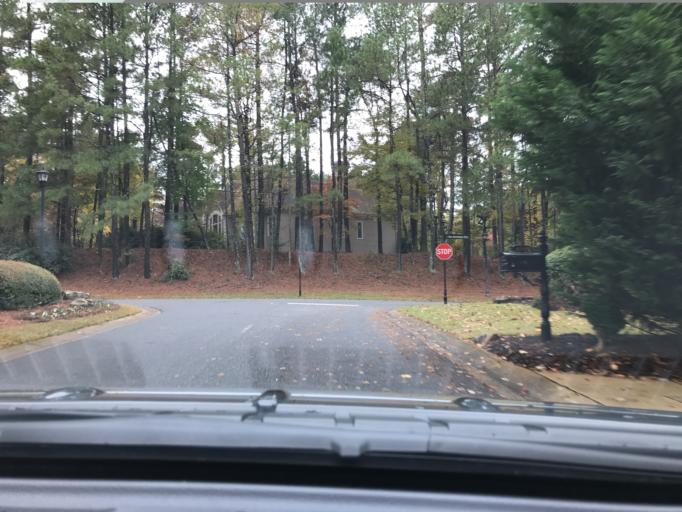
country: US
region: Georgia
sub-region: Fulton County
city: Johns Creek
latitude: 34.0121
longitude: -84.2341
